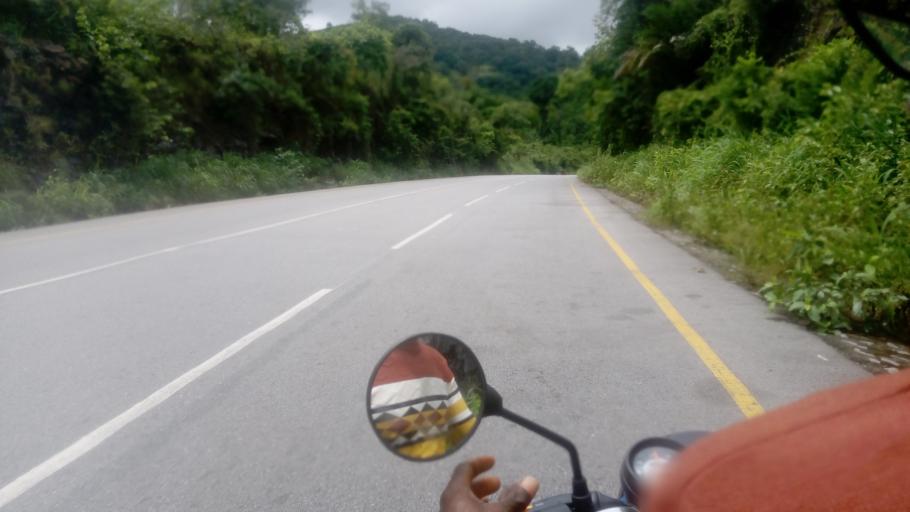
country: SL
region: Northern Province
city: Masaka
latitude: 8.6602
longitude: -11.7852
